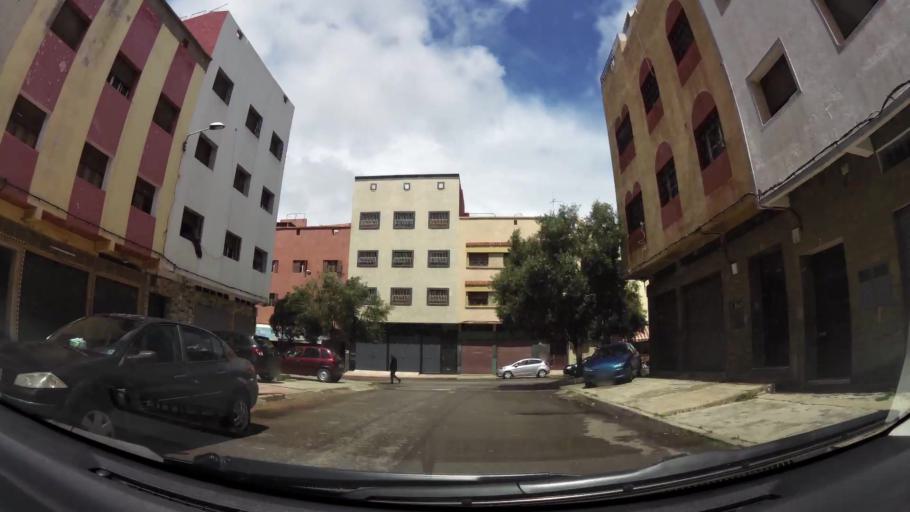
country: MA
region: Grand Casablanca
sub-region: Casablanca
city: Casablanca
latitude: 33.5530
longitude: -7.6795
